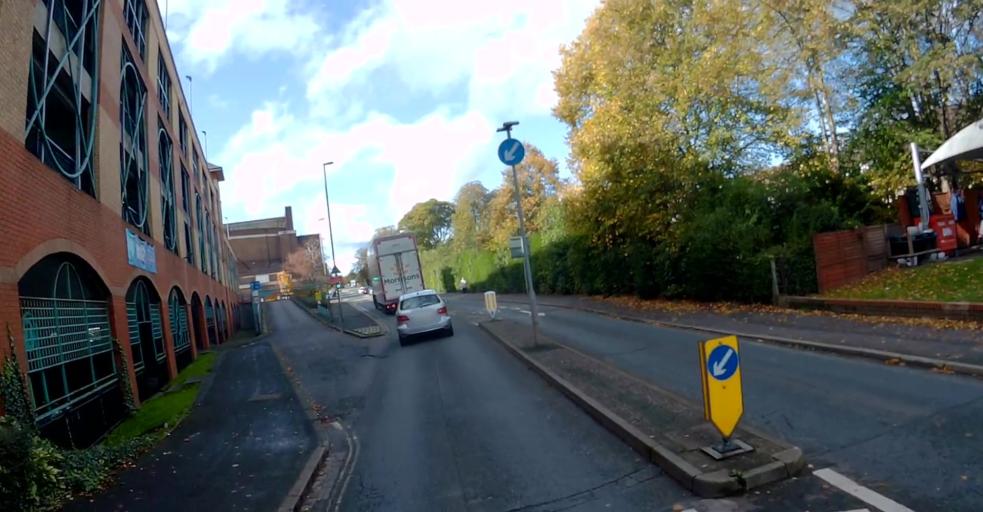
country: GB
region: England
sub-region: Hampshire
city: Aldershot
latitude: 51.2504
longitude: -0.7628
